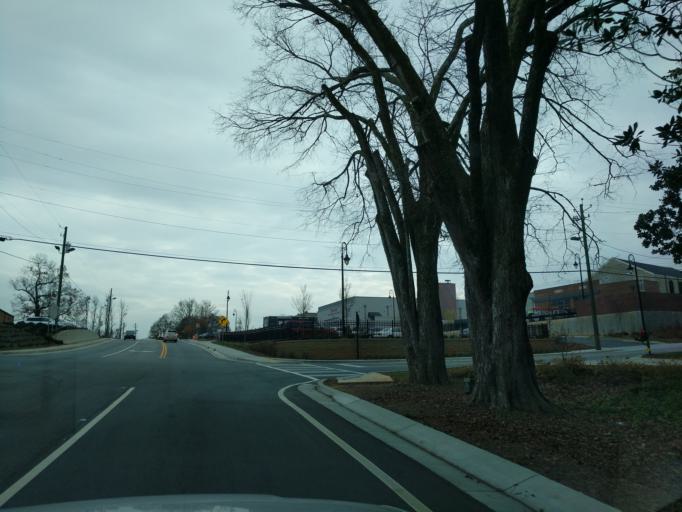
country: US
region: Georgia
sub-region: Gwinnett County
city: Duluth
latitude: 34.0046
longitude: -84.1445
